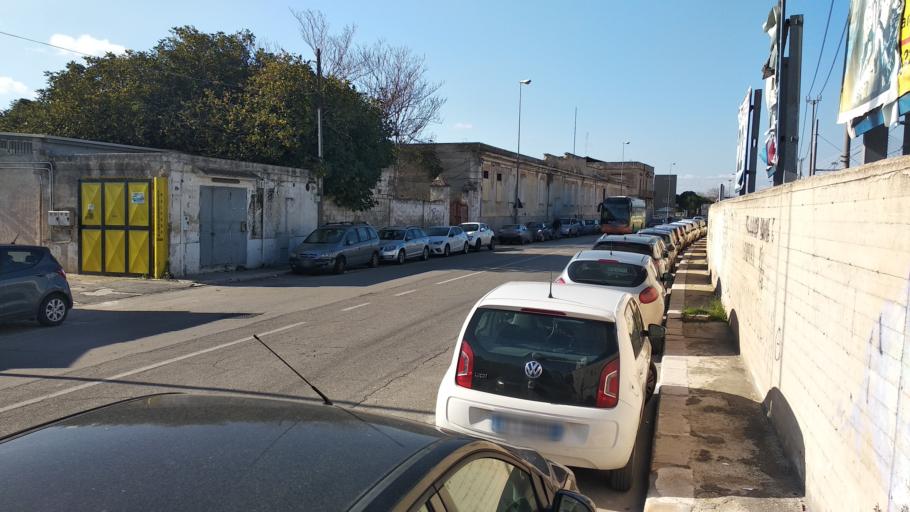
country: IT
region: Apulia
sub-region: Provincia di Bari
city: Bari
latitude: 41.1165
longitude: 16.8554
